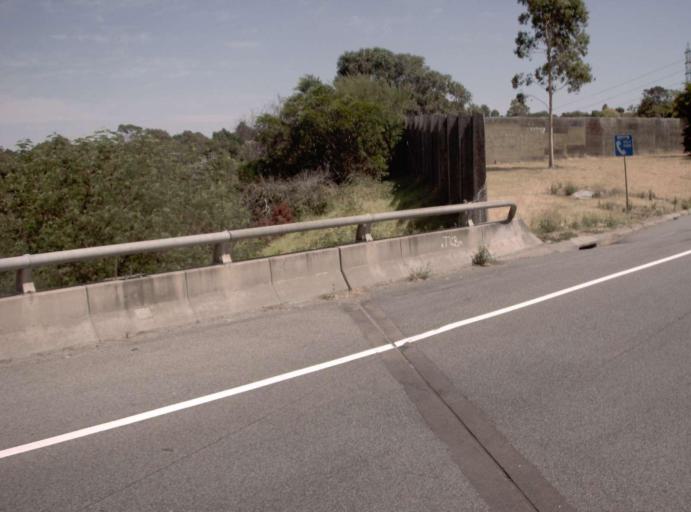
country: AU
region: Victoria
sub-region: Monash
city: Notting Hill
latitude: -37.9021
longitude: 145.1521
